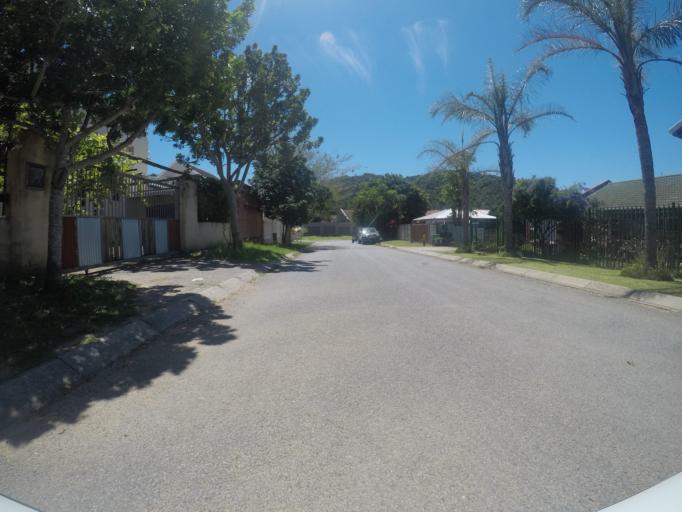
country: ZA
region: Eastern Cape
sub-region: Buffalo City Metropolitan Municipality
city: East London
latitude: -32.9282
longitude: 27.9975
